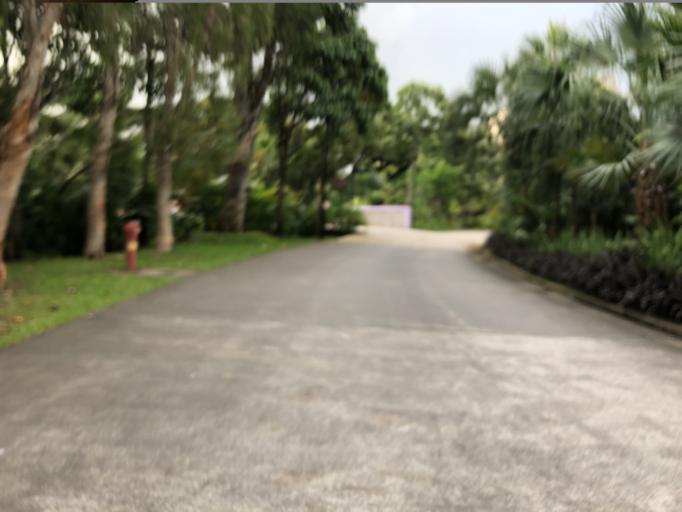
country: SG
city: Singapore
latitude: 1.2843
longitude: 103.8632
